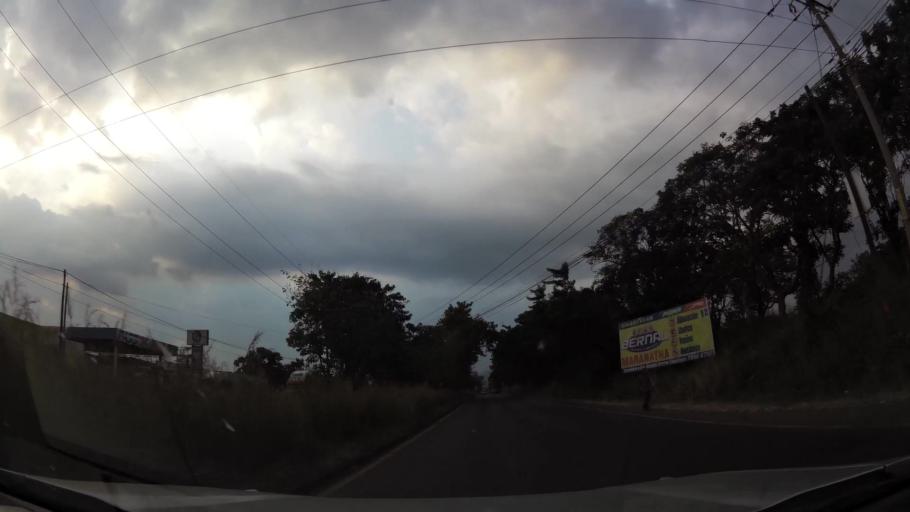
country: GT
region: Escuintla
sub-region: Municipio de Escuintla
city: Escuintla
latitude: 14.2773
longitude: -90.7787
